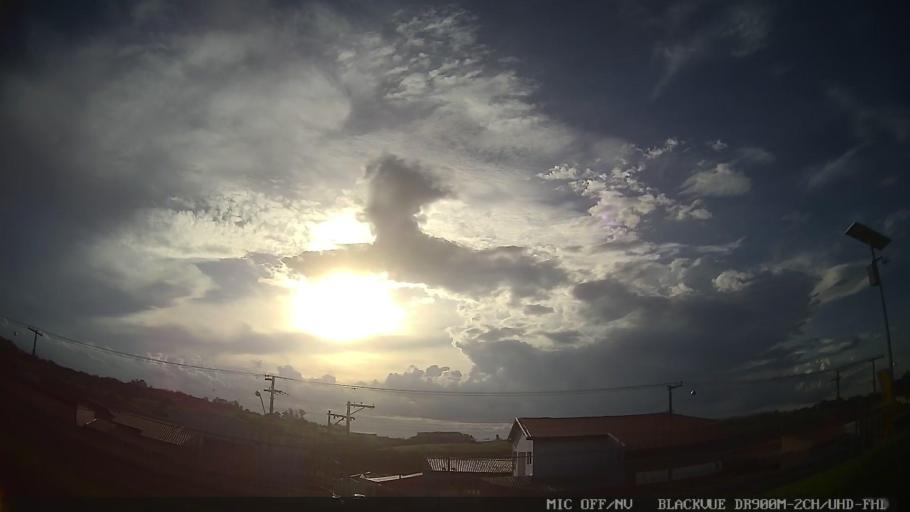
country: BR
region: Sao Paulo
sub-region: Tiete
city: Tiete
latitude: -23.1094
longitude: -47.7246
